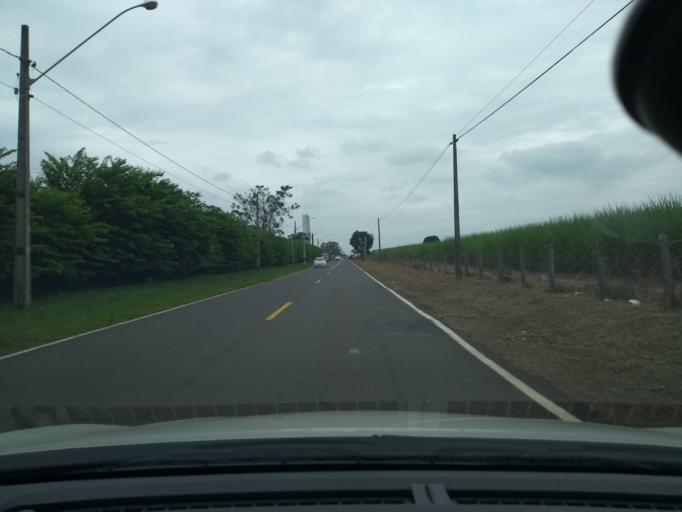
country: BR
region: Sao Paulo
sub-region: Rio Claro
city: Rio Claro
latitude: -22.3644
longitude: -47.5277
